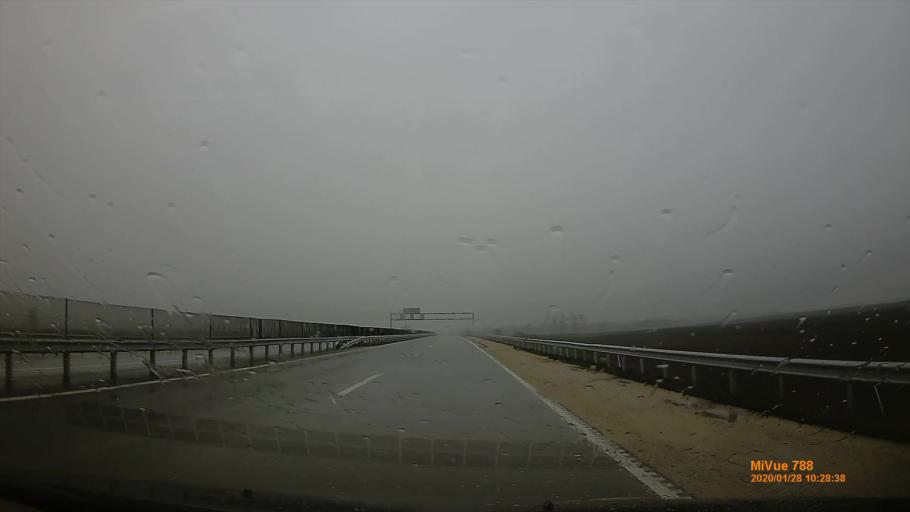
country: HU
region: Pest
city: Pilis
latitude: 47.3180
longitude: 19.5449
